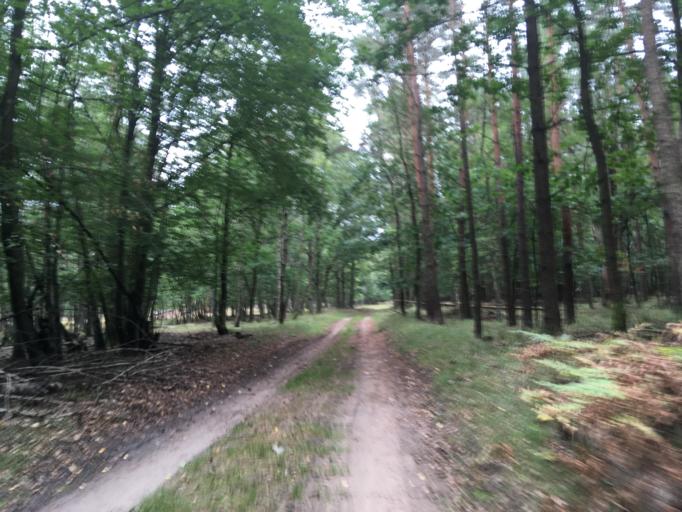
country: DE
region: Brandenburg
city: Zehdenick
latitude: 53.0403
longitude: 13.3334
